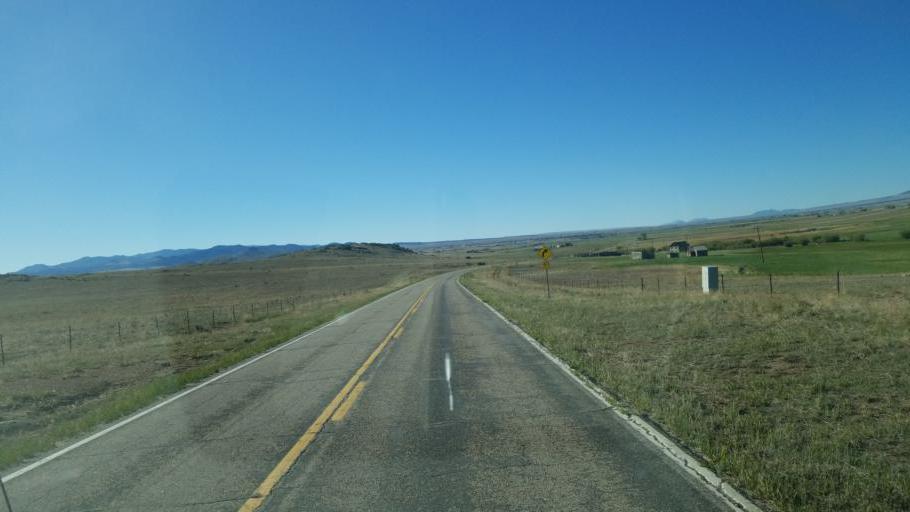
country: US
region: Colorado
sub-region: Custer County
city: Westcliffe
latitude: 38.1856
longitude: -105.5129
